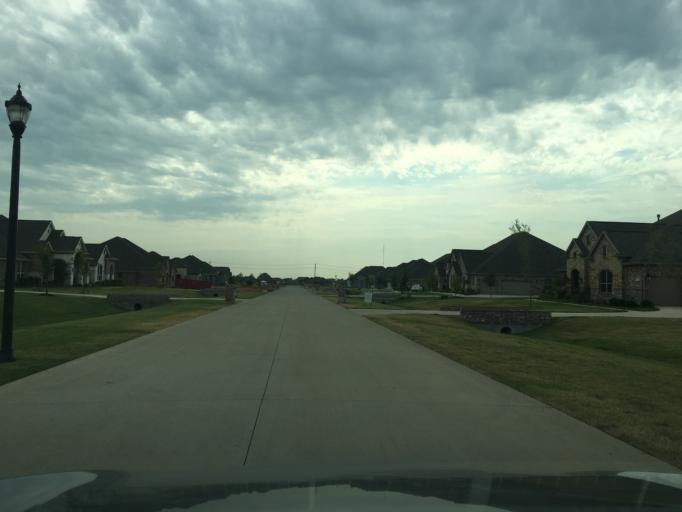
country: US
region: Texas
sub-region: Collin County
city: Parker
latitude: 33.0674
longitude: -96.6048
